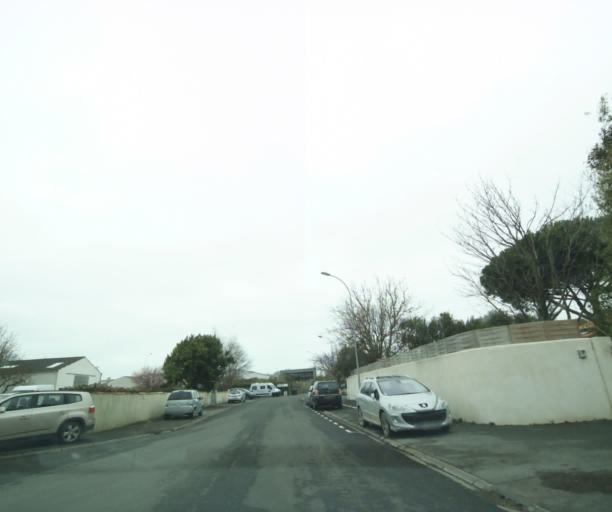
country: FR
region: Poitou-Charentes
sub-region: Departement de la Charente-Maritime
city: Lagord
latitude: 46.1880
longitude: -1.1445
